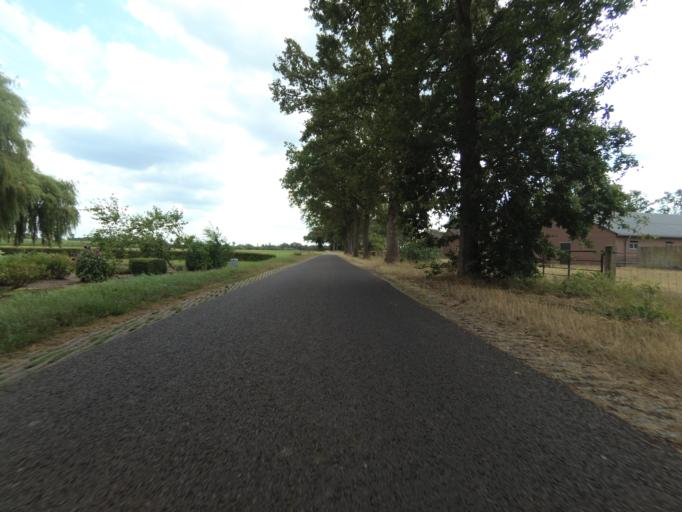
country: NL
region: Overijssel
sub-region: Gemeente Hof van Twente
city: Hengevelde
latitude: 52.1677
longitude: 6.6820
